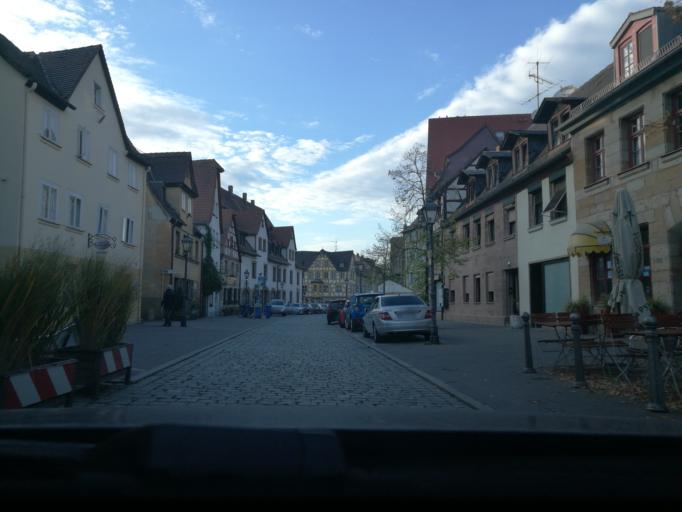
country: DE
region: Bavaria
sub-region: Regierungsbezirk Mittelfranken
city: Furth
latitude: 49.4793
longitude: 10.9884
